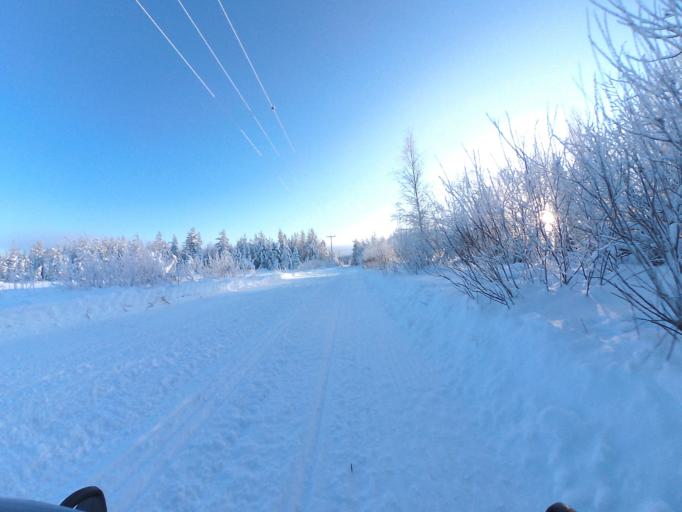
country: FI
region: Lapland
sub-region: Rovaniemi
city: Rovaniemi
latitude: 66.5450
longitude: 25.8648
